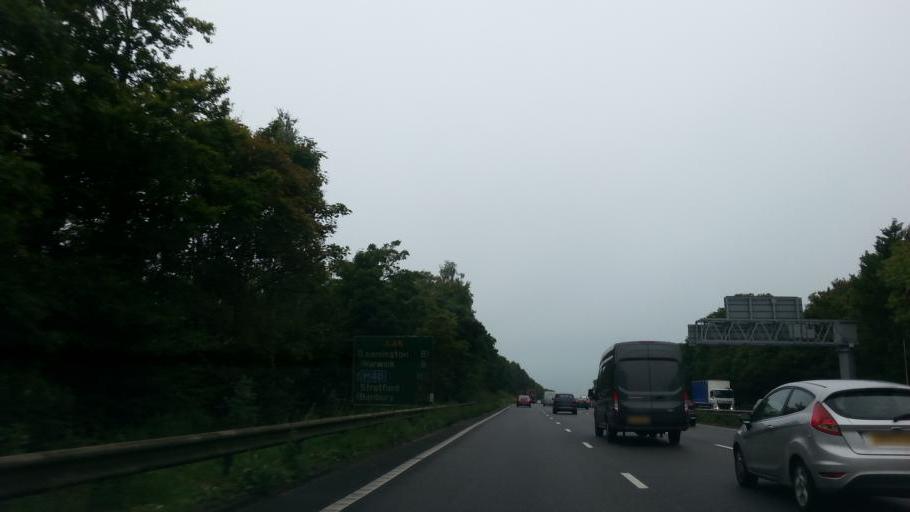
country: GB
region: England
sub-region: Coventry
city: Coventry
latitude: 52.3726
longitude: -1.5091
